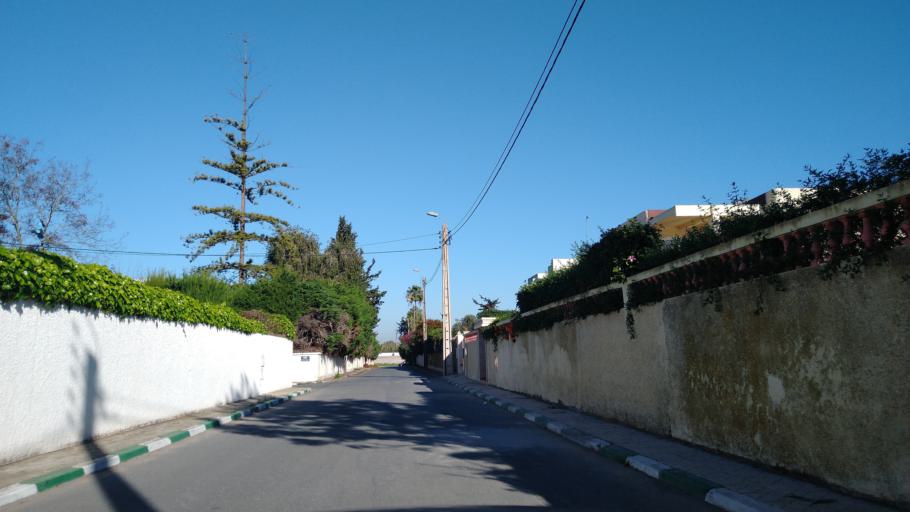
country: MA
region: Rabat-Sale-Zemmour-Zaer
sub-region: Rabat
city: Rabat
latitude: 33.9588
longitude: -6.8376
